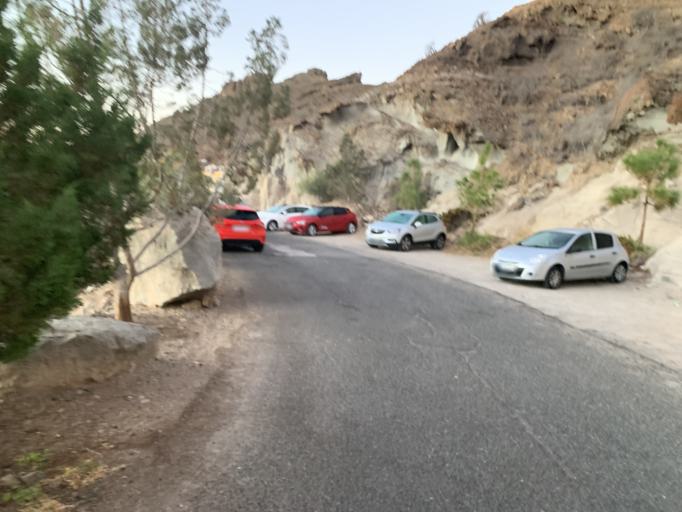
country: ES
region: Canary Islands
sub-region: Provincia de Las Palmas
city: Puerto Rico
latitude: 27.8048
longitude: -15.7331
